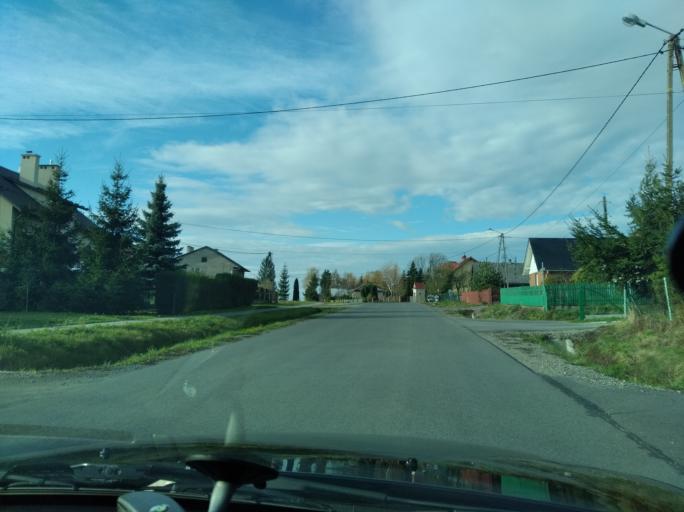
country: PL
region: Subcarpathian Voivodeship
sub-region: Powiat ropczycko-sedziszowski
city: Sedziszow Malopolski
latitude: 50.0806
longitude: 21.7296
